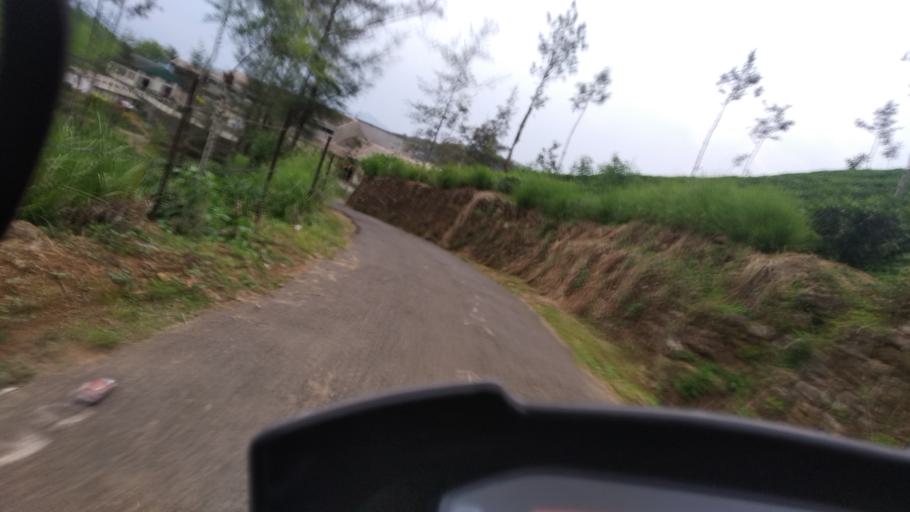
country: IN
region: Tamil Nadu
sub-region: Theni
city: Gudalur
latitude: 9.5413
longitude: 77.0417
